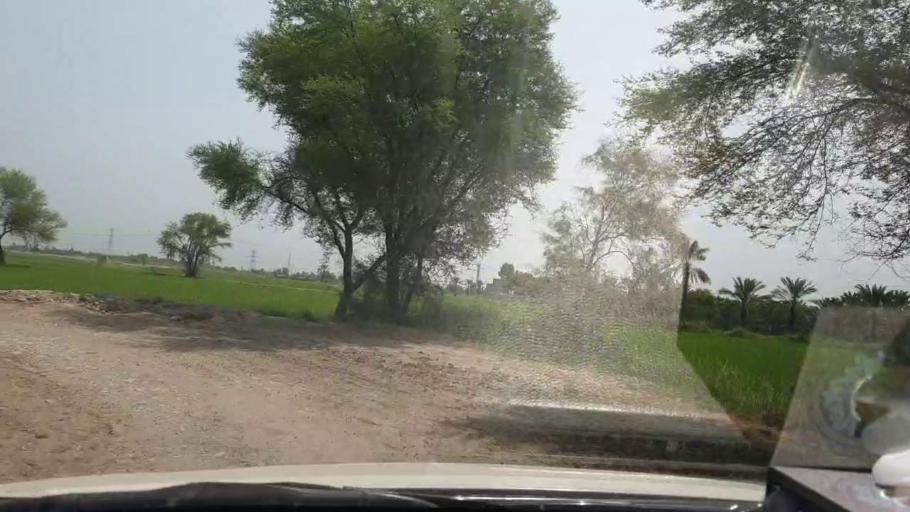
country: PK
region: Sindh
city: Shikarpur
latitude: 27.9902
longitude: 68.6967
